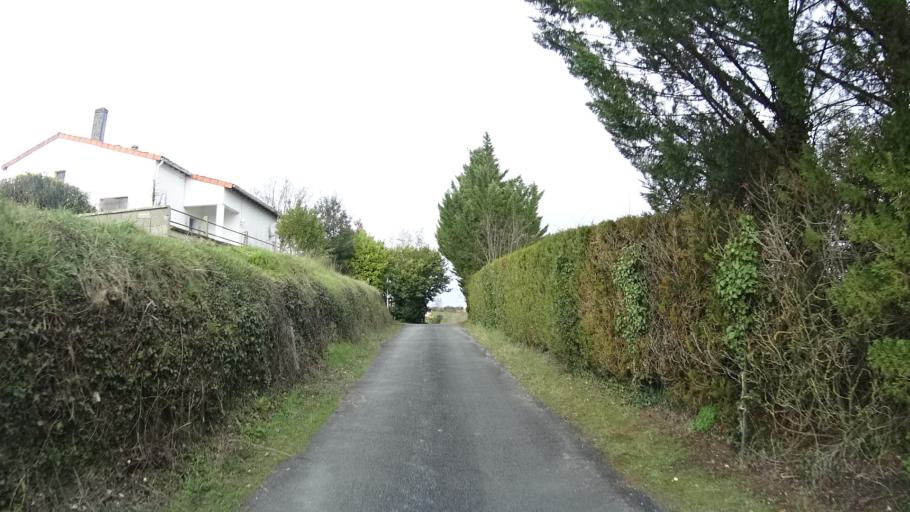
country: FR
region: Aquitaine
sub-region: Departement de la Dordogne
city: Saint-Aulaye
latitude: 45.2433
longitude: 0.1498
